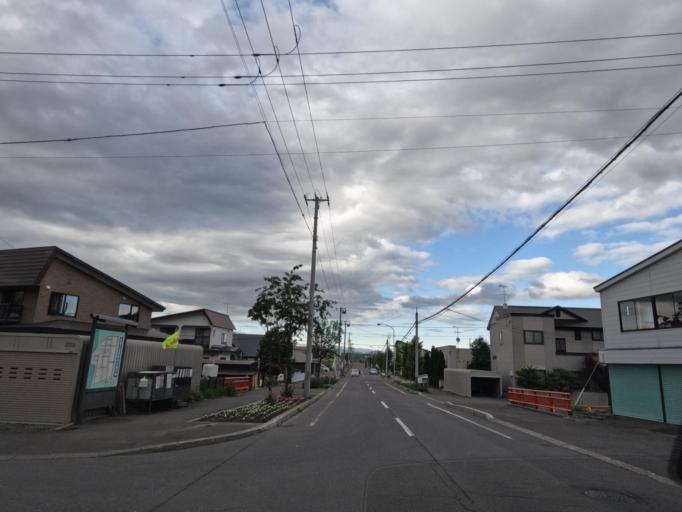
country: JP
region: Hokkaido
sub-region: Asahikawa-shi
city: Asahikawa
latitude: 43.7722
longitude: 142.3118
